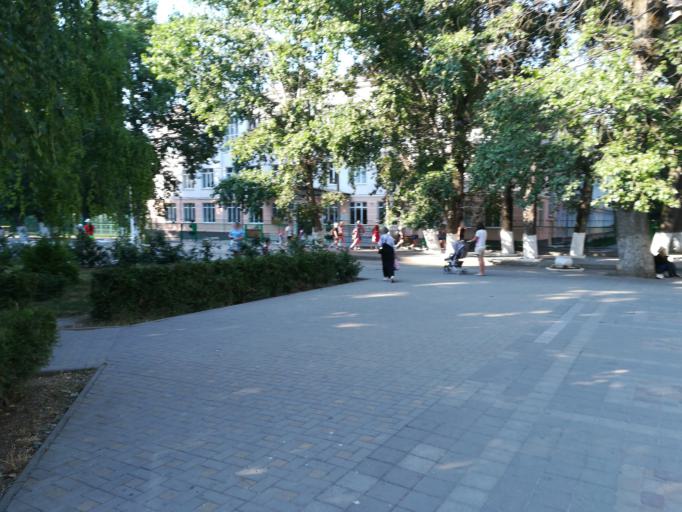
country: RU
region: Krasnodarskiy
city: Anapa
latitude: 44.9009
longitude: 37.3321
